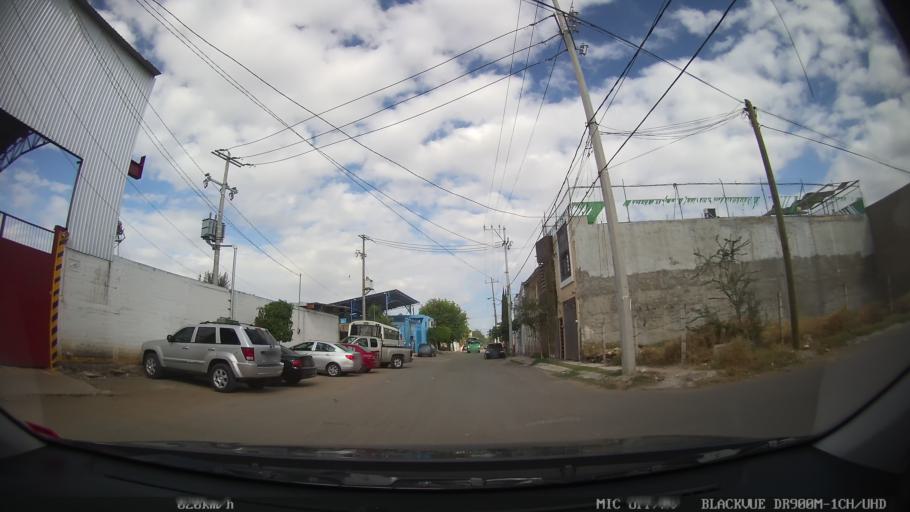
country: MX
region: Jalisco
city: Tonala
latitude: 20.6597
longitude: -103.2363
